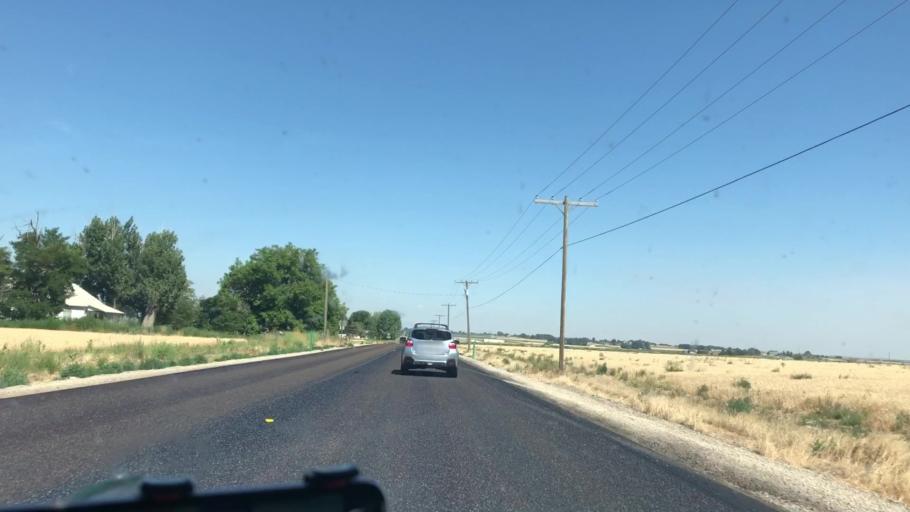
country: US
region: Idaho
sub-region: Owyhee County
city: Marsing
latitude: 43.6031
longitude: -116.7712
